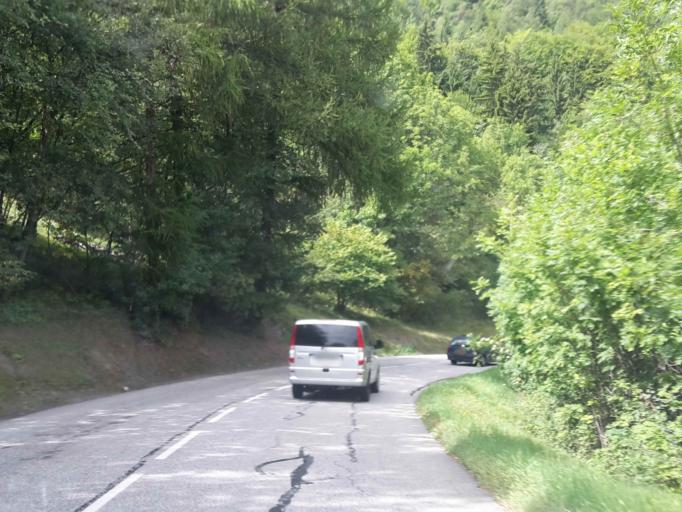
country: FR
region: Rhone-Alpes
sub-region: Departement de la Savoie
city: Saint-Michel-de-Maurienne
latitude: 45.2096
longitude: 6.4560
